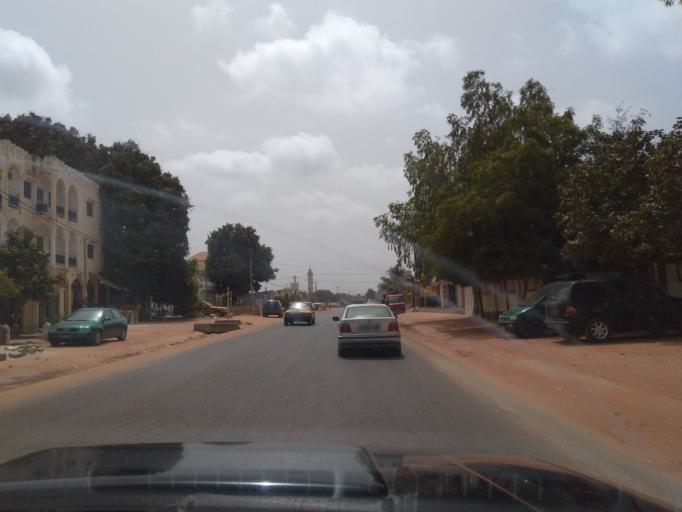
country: GM
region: Western
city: Sukuta
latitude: 13.4411
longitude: -16.7094
